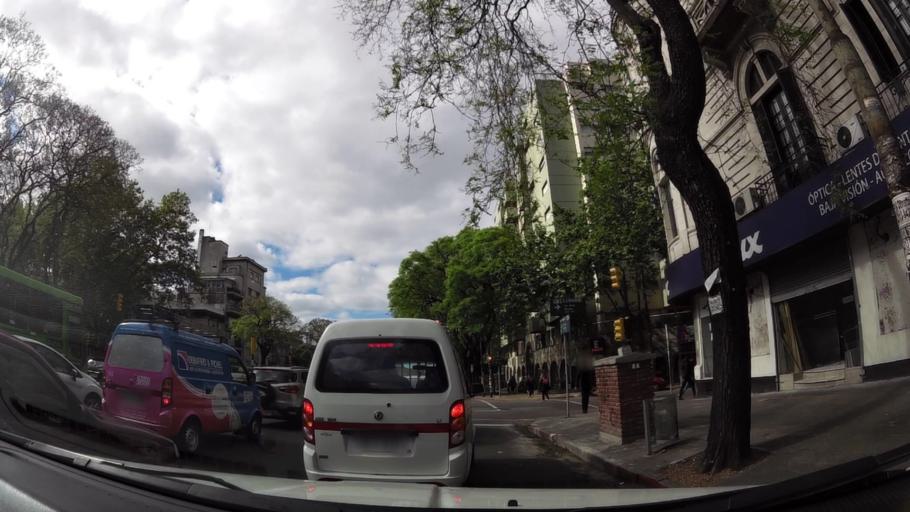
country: UY
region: Montevideo
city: Montevideo
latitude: -34.9020
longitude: -56.1643
